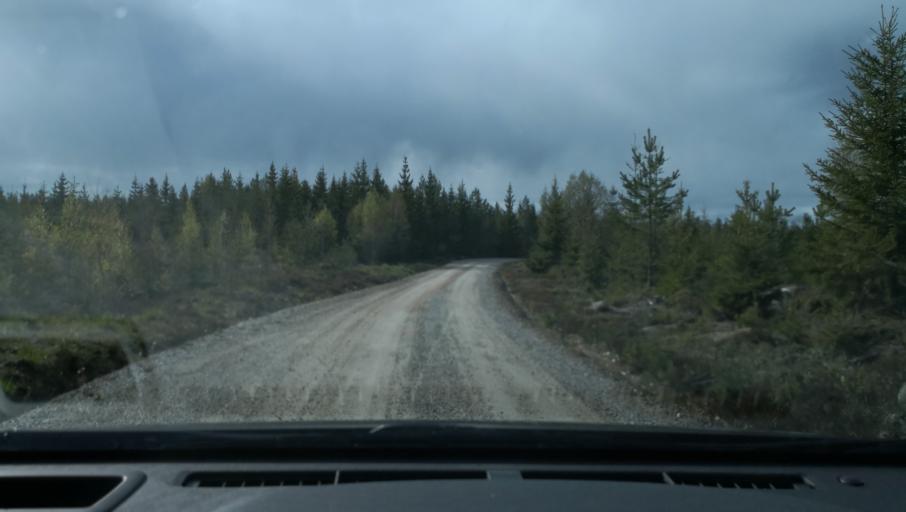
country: SE
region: Vaestmanland
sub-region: Fagersta Kommun
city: Fagersta
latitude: 60.1683
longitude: 15.7214
